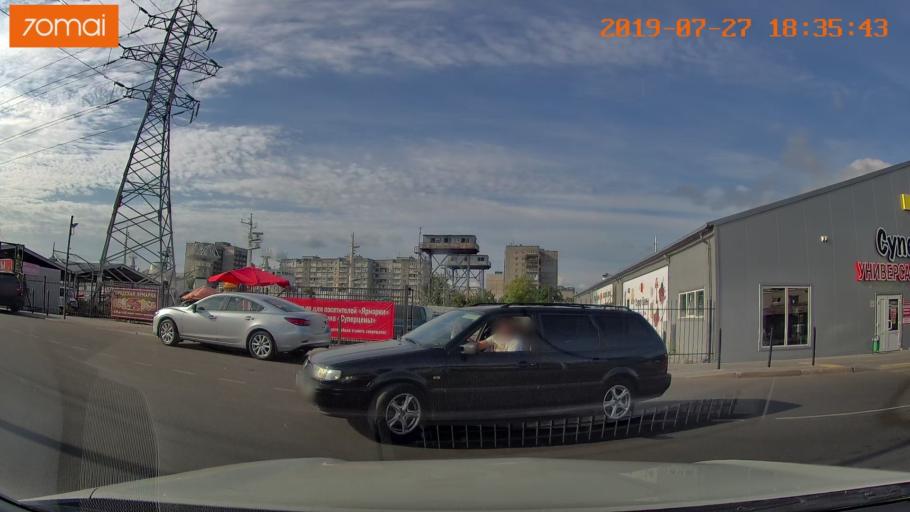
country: RU
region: Kaliningrad
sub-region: Gorod Kaliningrad
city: Kaliningrad
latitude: 54.7049
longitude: 20.4981
